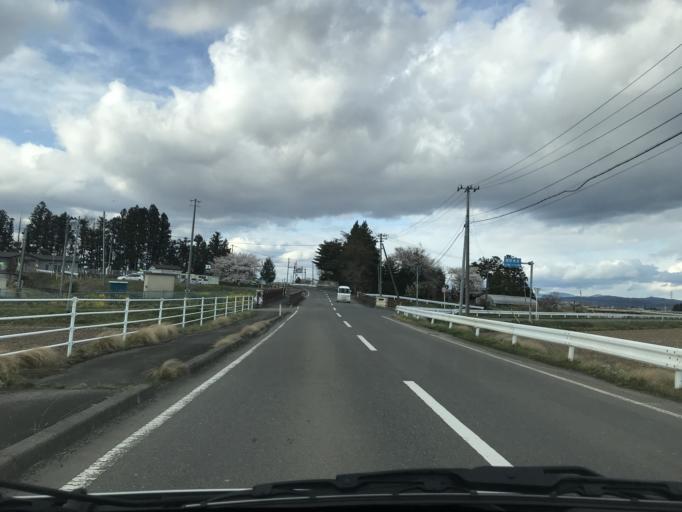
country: JP
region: Miyagi
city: Wakuya
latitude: 38.6464
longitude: 141.2166
